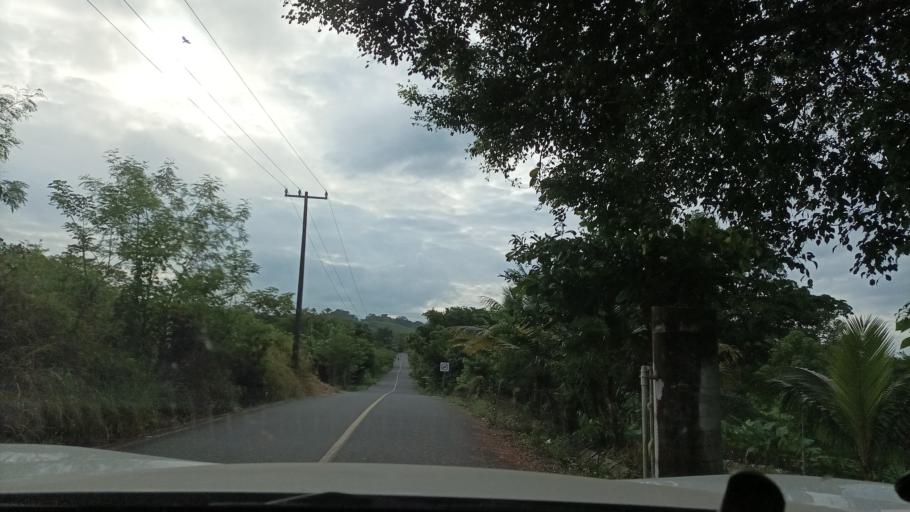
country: MX
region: Veracruz
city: Hidalgotitlan
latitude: 17.7135
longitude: -94.4715
